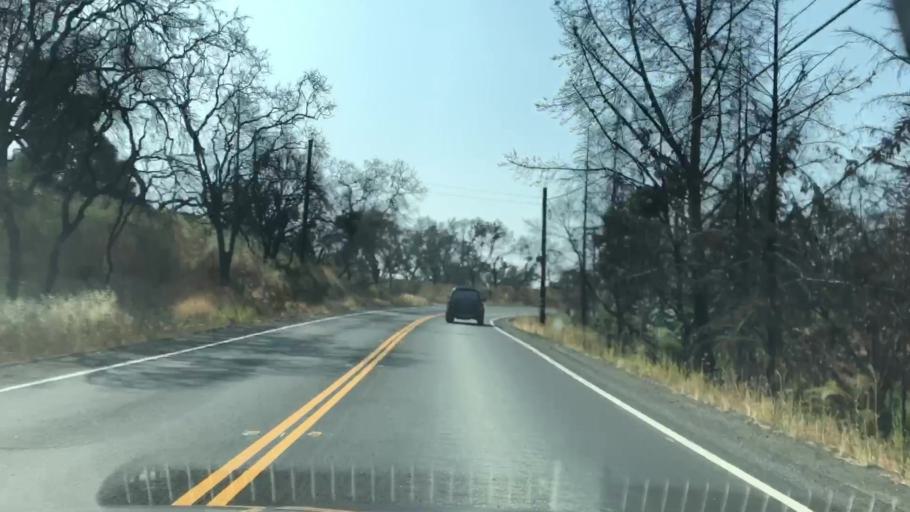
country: US
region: California
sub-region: Sonoma County
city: Larkfield-Wikiup
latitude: 38.5221
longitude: -122.7186
